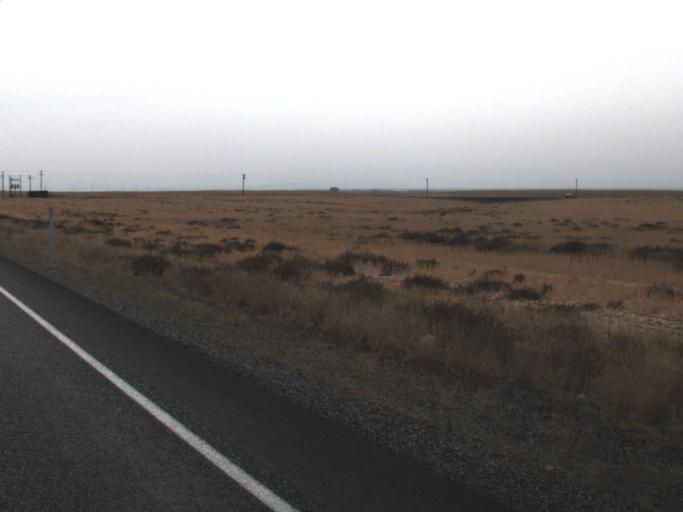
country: US
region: Washington
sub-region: Benton County
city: Benton City
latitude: 46.1348
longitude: -119.6014
